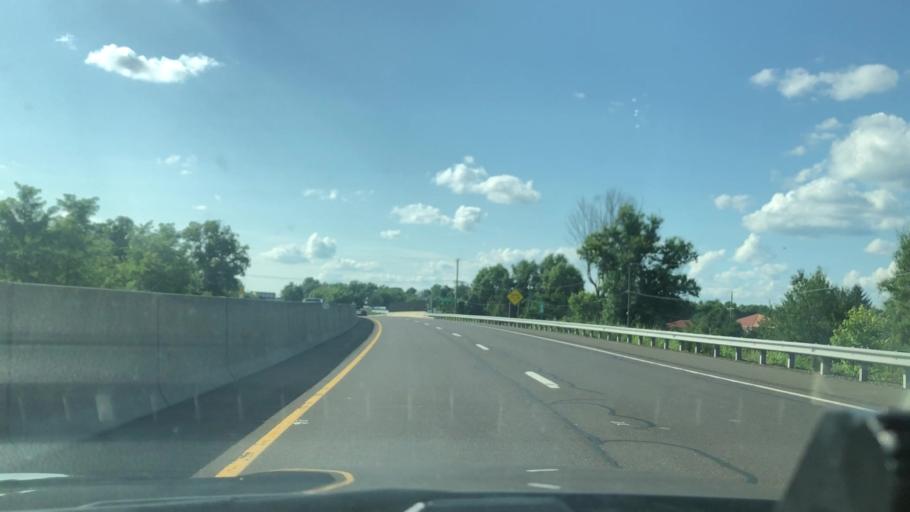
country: US
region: Pennsylvania
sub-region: Montgomery County
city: Spring House
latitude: 40.1894
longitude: -75.2139
